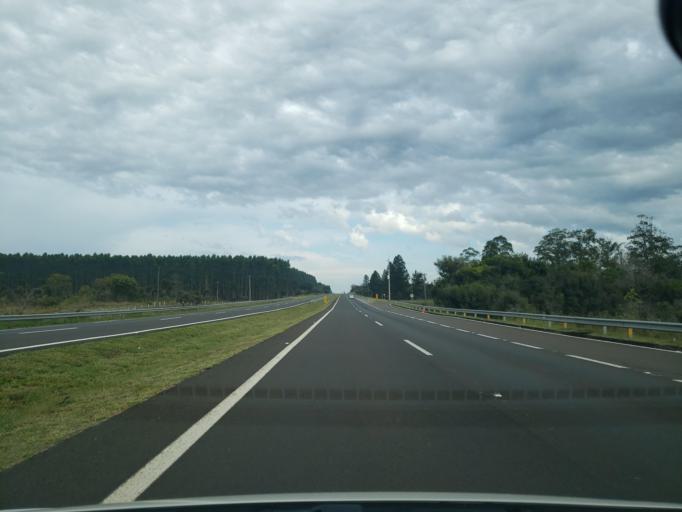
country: BR
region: Sao Paulo
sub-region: Itirapina
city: Itirapina
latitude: -22.2581
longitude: -47.8650
